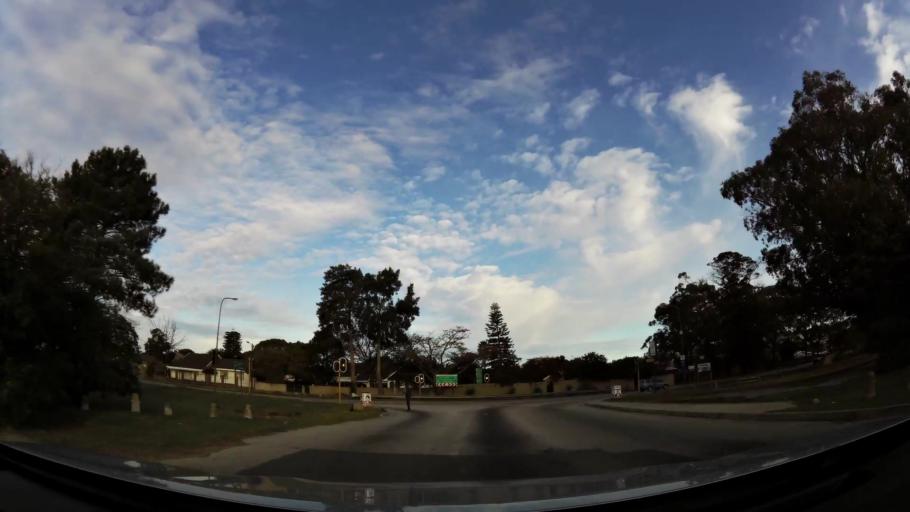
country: ZA
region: Eastern Cape
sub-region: Nelson Mandela Bay Metropolitan Municipality
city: Port Elizabeth
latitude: -33.9547
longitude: 25.5198
